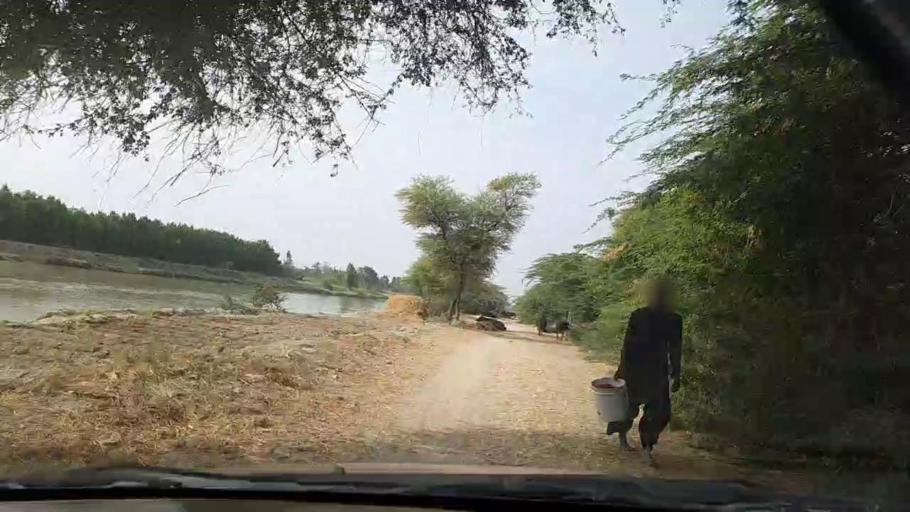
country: PK
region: Sindh
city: Thatta
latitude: 24.5710
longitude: 67.8562
